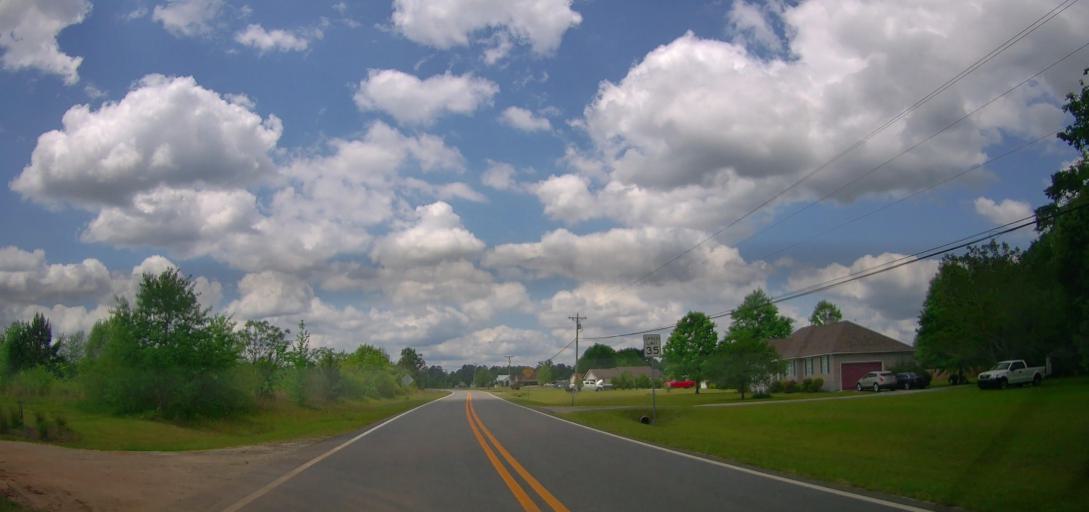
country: US
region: Georgia
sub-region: Laurens County
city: Dublin
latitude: 32.6002
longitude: -82.9581
